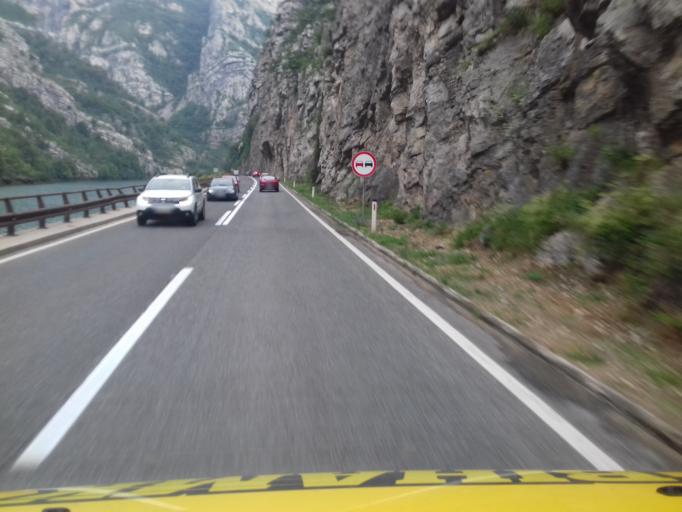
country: BA
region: Federation of Bosnia and Herzegovina
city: Jablanica
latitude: 43.6116
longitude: 17.7395
